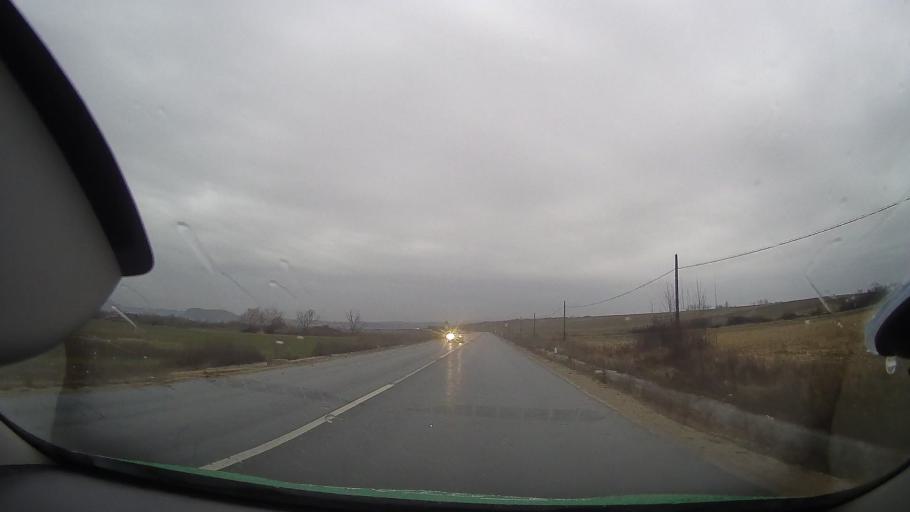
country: RO
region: Bihor
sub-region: Municipiul Beius
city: Beius
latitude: 46.6774
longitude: 22.3198
